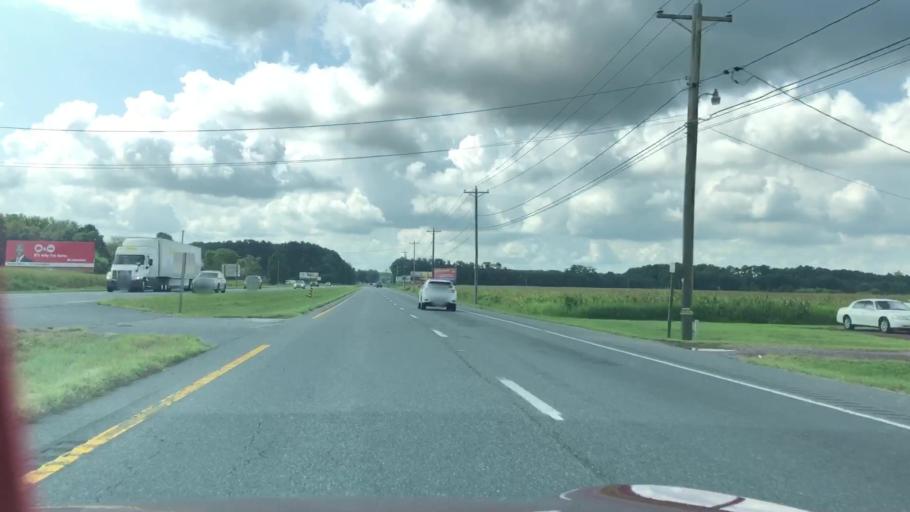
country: US
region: Virginia
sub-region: Accomack County
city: Wattsville
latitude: 37.9699
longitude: -75.5324
